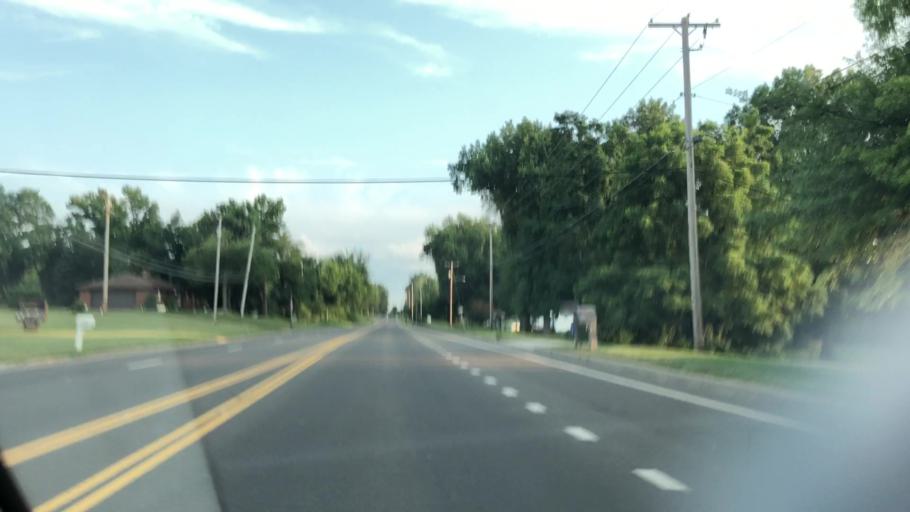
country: US
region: Ohio
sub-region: Summit County
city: Greensburg
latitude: 40.8767
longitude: -81.4798
